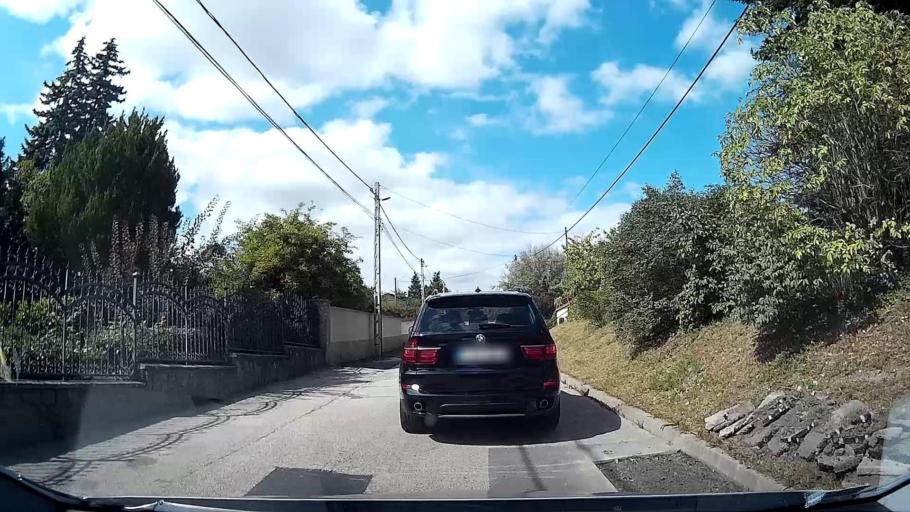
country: HU
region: Pest
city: Szentendre
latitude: 47.6876
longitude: 19.0734
